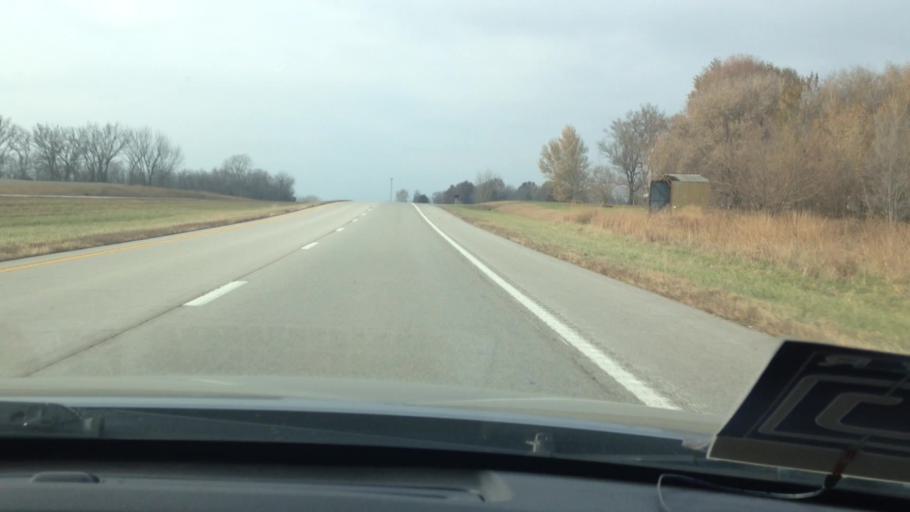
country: US
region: Missouri
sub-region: Cass County
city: Garden City
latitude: 38.5418
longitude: -94.1630
